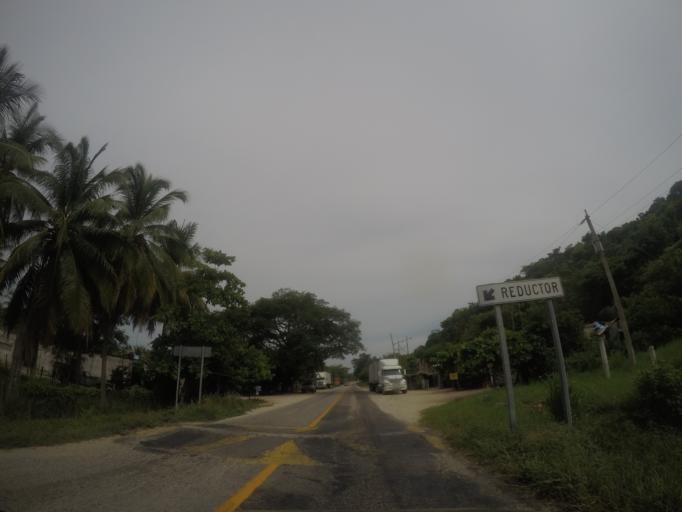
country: MX
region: Oaxaca
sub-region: Villa de Tututepec de Melchor Ocampo
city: Santa Rosa de Lima
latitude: 15.9696
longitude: -97.3970
